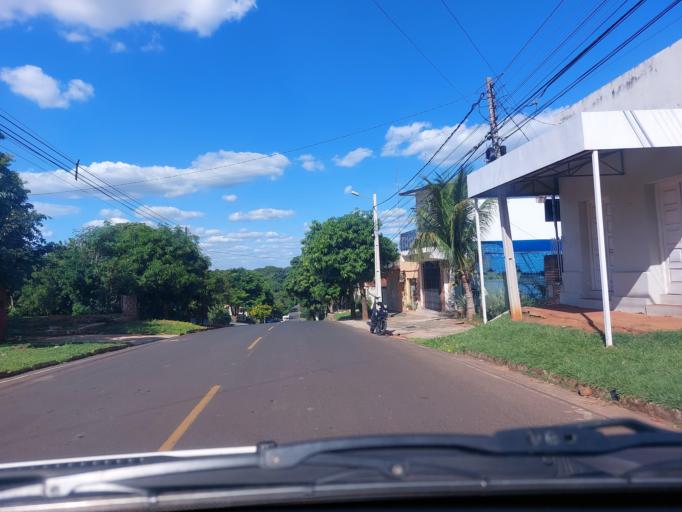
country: PY
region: San Pedro
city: Guayaybi
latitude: -24.6642
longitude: -56.4517
